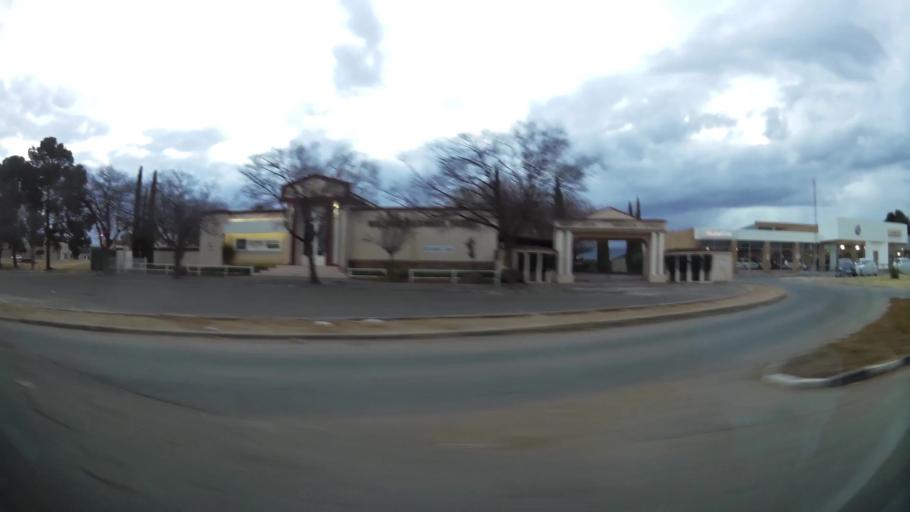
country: ZA
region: Orange Free State
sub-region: Lejweleputswa District Municipality
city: Welkom
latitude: -27.9782
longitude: 26.7439
